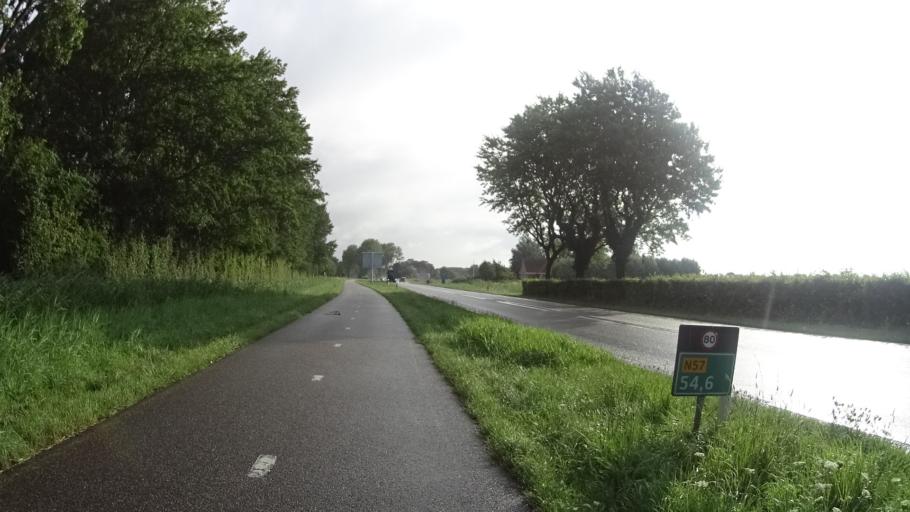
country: NL
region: Zeeland
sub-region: Schouwen-Duiveland
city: Burgh
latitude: 51.6833
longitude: 3.7299
